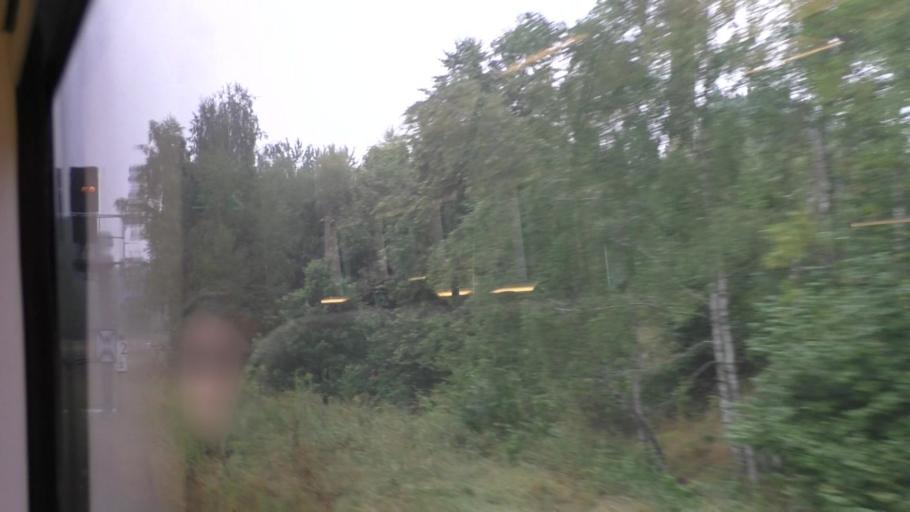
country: CZ
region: Ustecky
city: Jirikov
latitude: 50.9968
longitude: 14.5804
